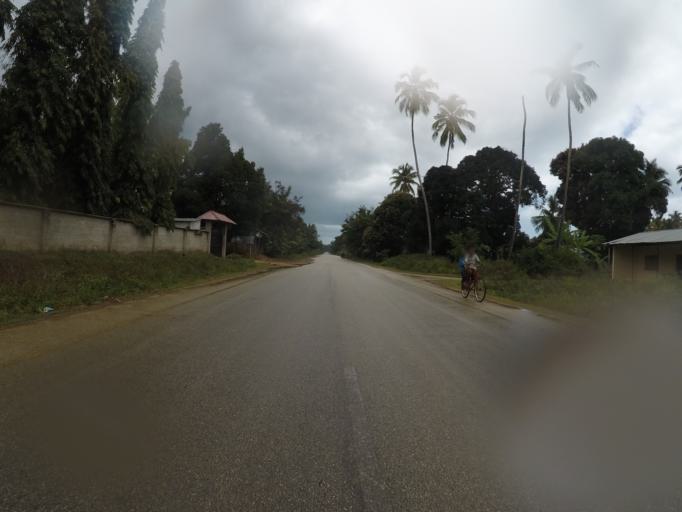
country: TZ
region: Zanzibar North
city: Mkokotoni
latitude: -5.9757
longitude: 39.1962
